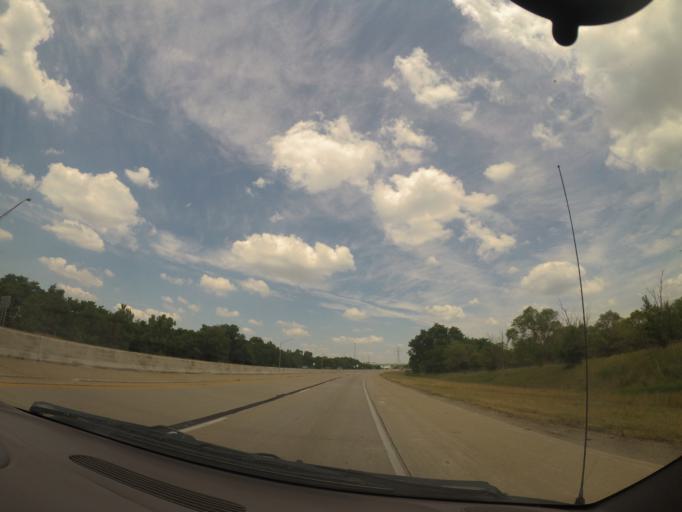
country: US
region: Indiana
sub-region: Elkhart County
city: Dunlap
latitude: 41.6636
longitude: -85.8993
